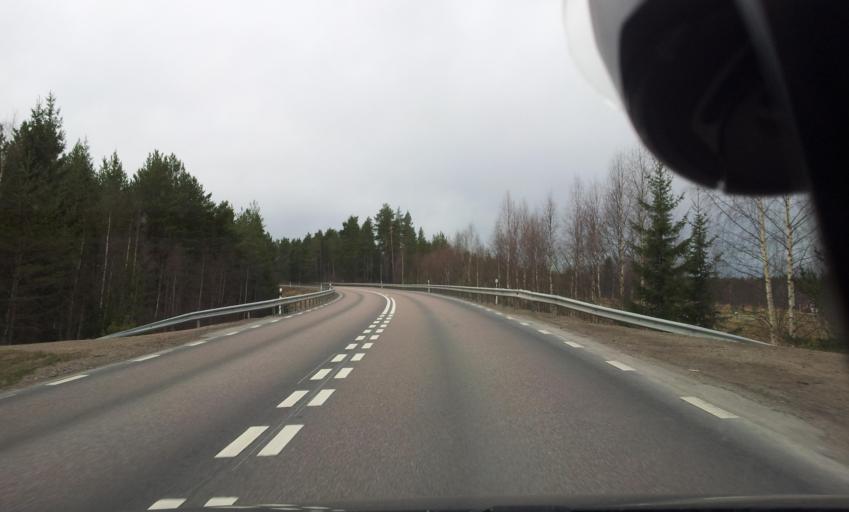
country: SE
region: Gaevleborg
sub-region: Ljusdals Kommun
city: Ljusdal
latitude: 61.8246
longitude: 16.0323
